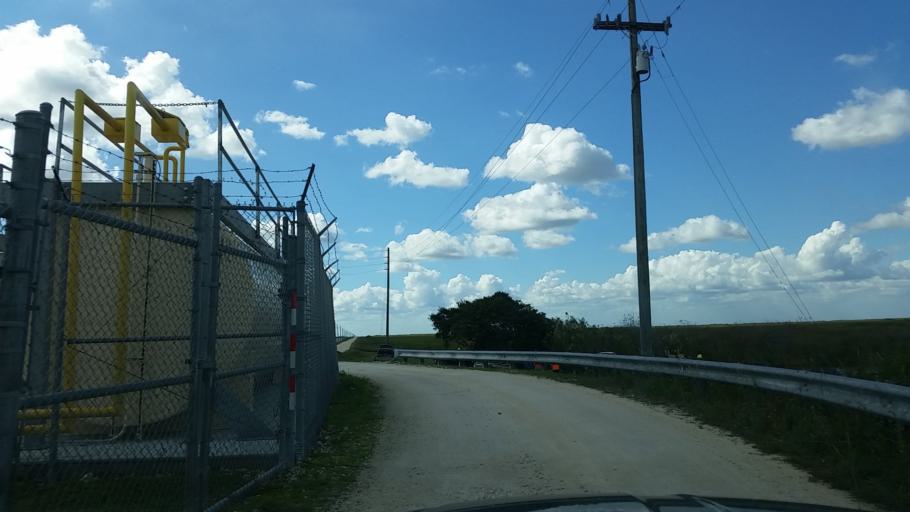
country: US
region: Florida
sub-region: Miami-Dade County
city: Kendall West
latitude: 25.7617
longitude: -80.5018
